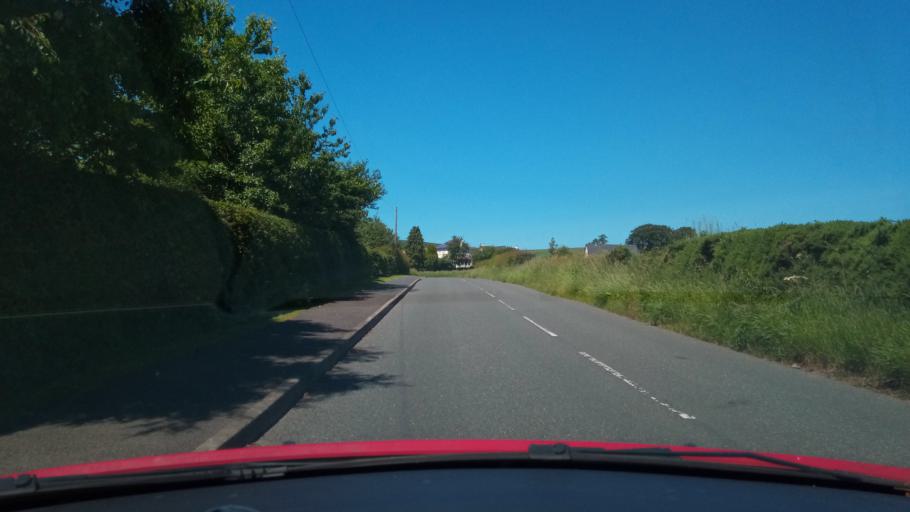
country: GB
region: Scotland
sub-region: The Scottish Borders
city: Duns
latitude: 55.7724
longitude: -2.3659
